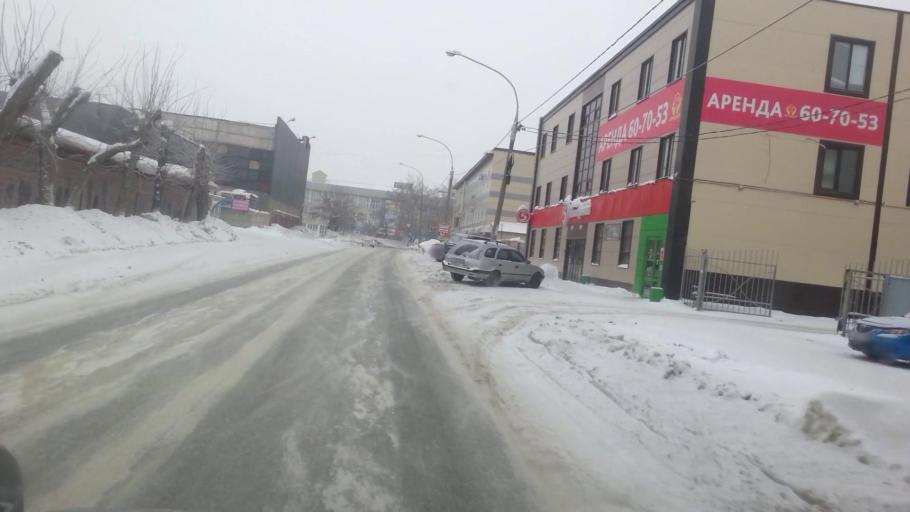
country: RU
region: Altai Krai
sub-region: Gorod Barnaulskiy
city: Barnaul
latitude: 53.3823
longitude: 83.7371
